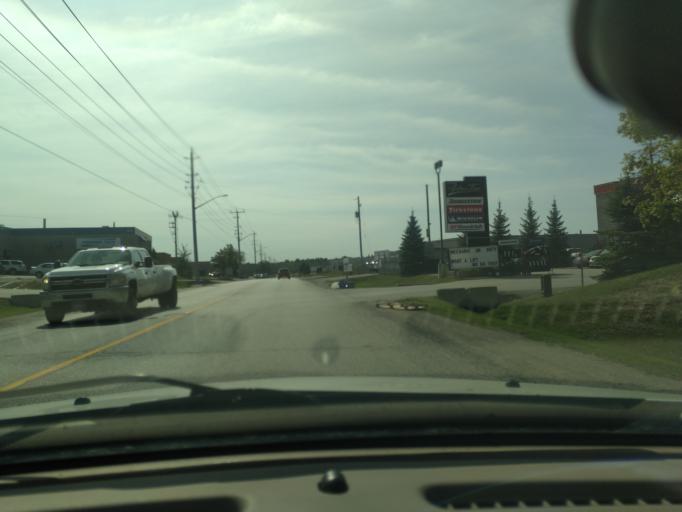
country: CA
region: Ontario
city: Innisfil
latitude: 44.3307
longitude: -79.6773
